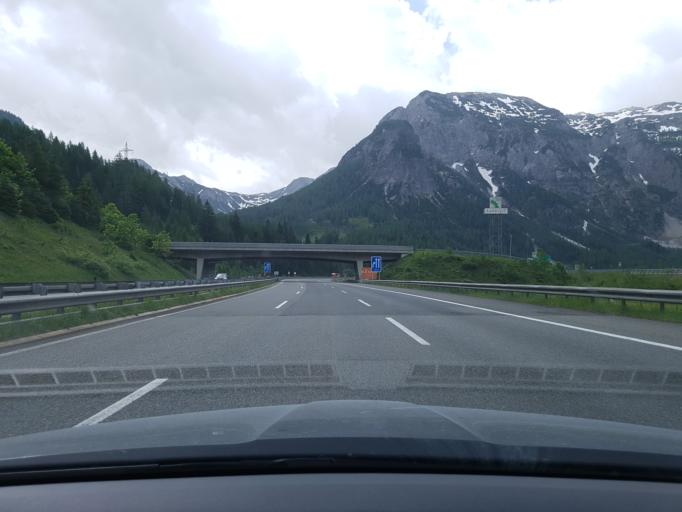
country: AT
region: Salzburg
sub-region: Politischer Bezirk Sankt Johann im Pongau
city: Untertauern
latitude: 47.2489
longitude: 13.4233
